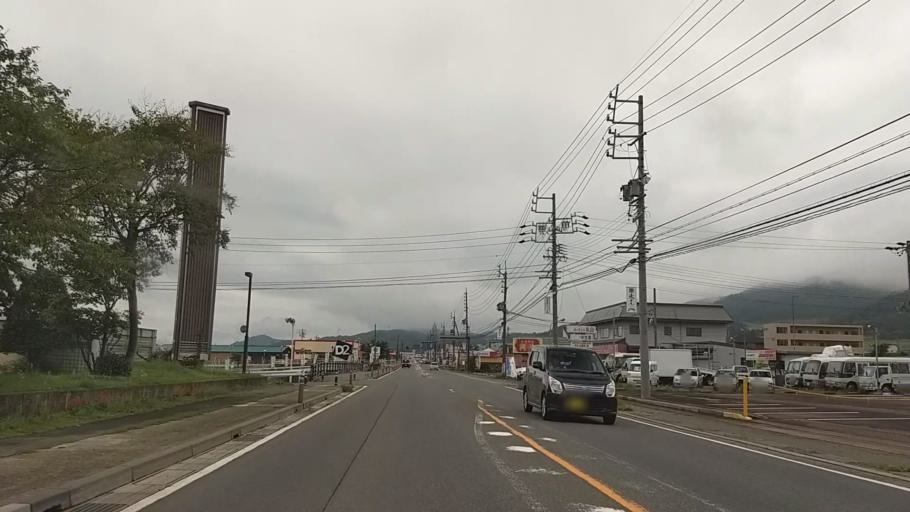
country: JP
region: Nagano
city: Iiyama
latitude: 36.8370
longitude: 138.3586
